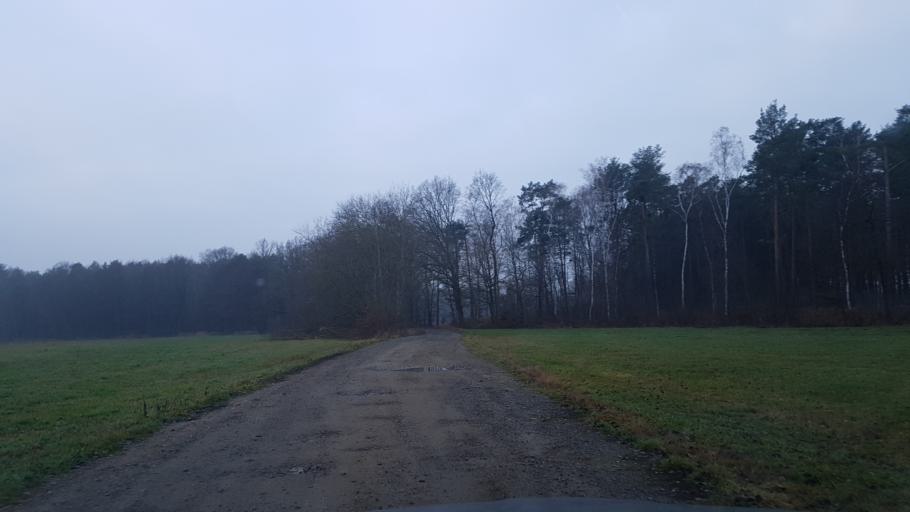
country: DE
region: Brandenburg
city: Ruckersdorf
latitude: 51.5559
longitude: 13.5744
